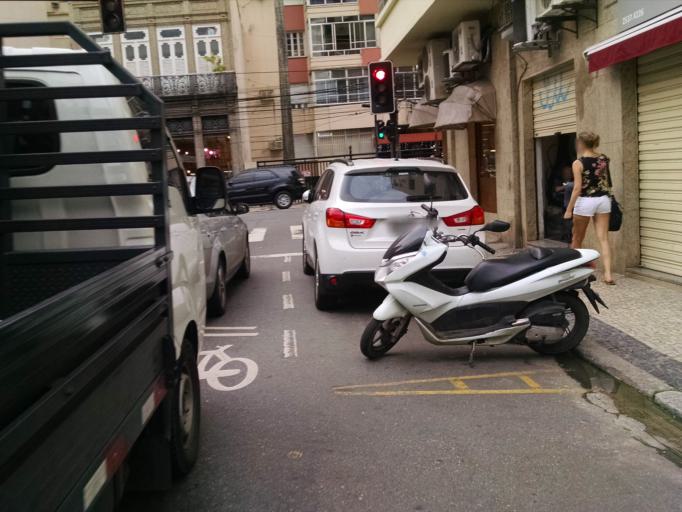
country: BR
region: Rio de Janeiro
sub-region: Rio De Janeiro
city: Rio de Janeiro
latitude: -22.9439
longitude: -43.1852
